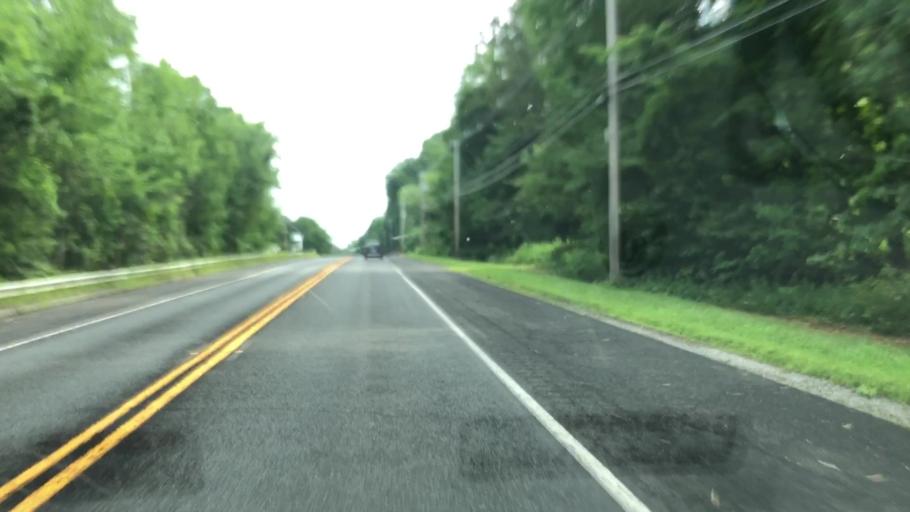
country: US
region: Massachusetts
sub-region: Berkshire County
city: Lanesborough
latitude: 42.5424
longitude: -73.1723
